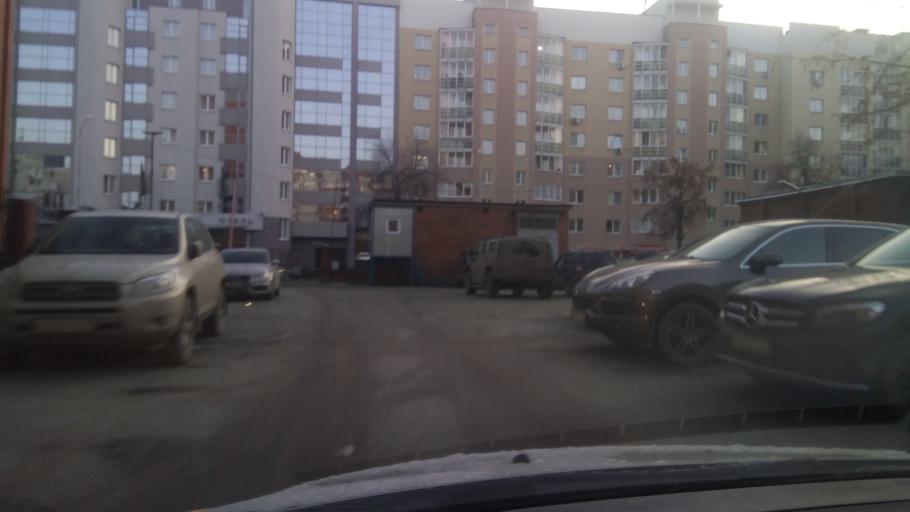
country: RU
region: Sverdlovsk
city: Yekaterinburg
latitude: 56.8384
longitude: 60.5477
